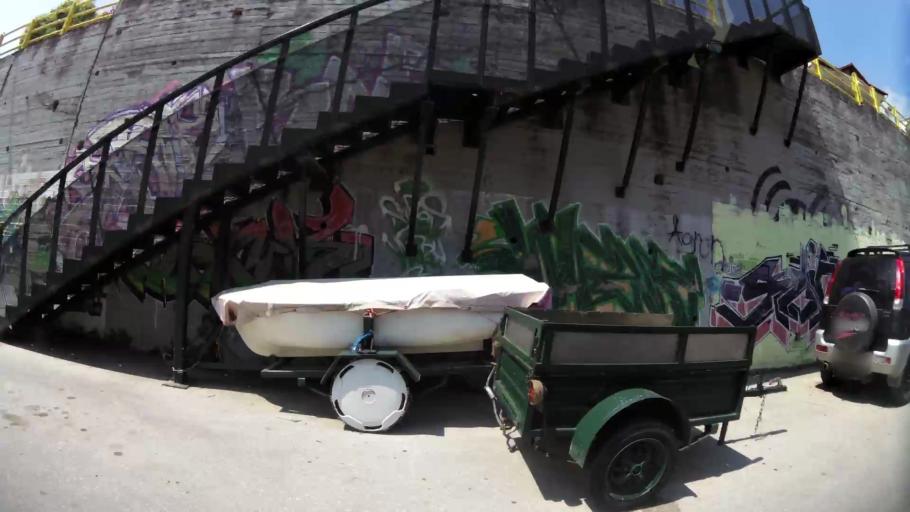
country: GR
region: Central Macedonia
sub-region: Nomos Imathias
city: Veroia
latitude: 40.5107
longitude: 22.2131
